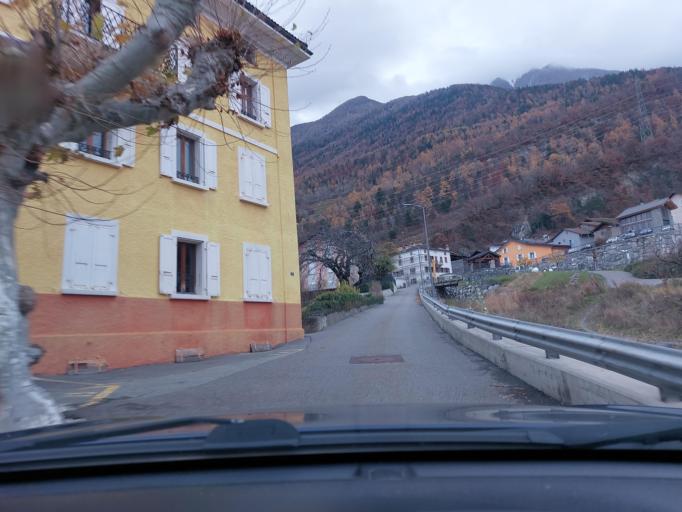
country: CH
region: Valais
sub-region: Martigny District
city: Saxon
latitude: 46.1459
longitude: 7.1786
